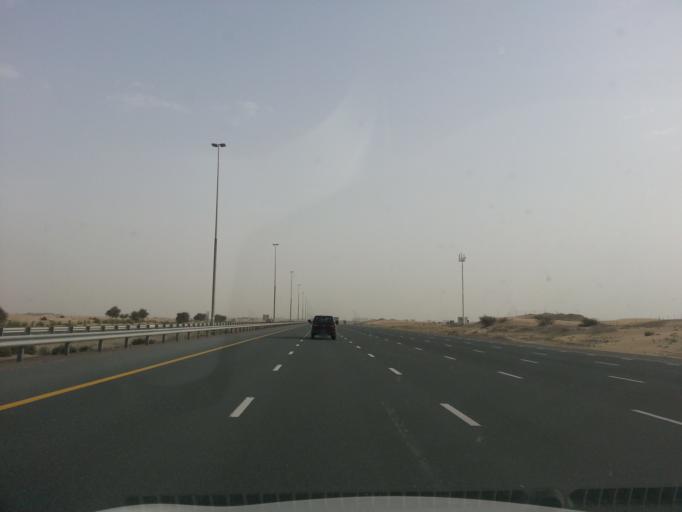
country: AE
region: Dubai
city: Dubai
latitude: 24.9730
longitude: 55.2389
